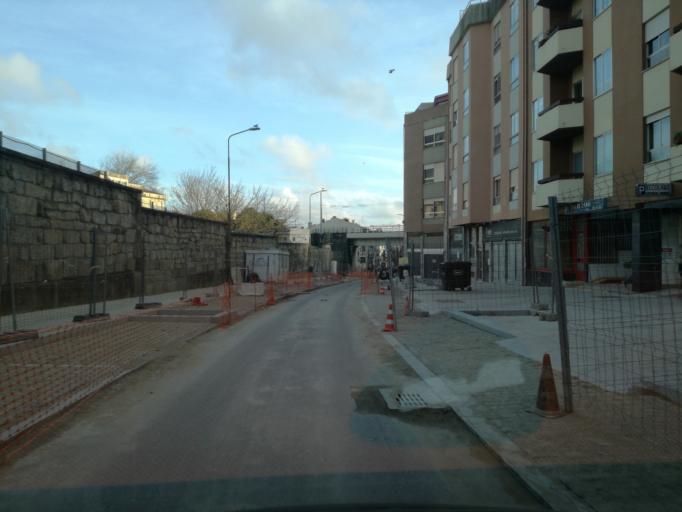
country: PT
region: Porto
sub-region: Porto
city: Porto
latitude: 41.1589
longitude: -8.6201
